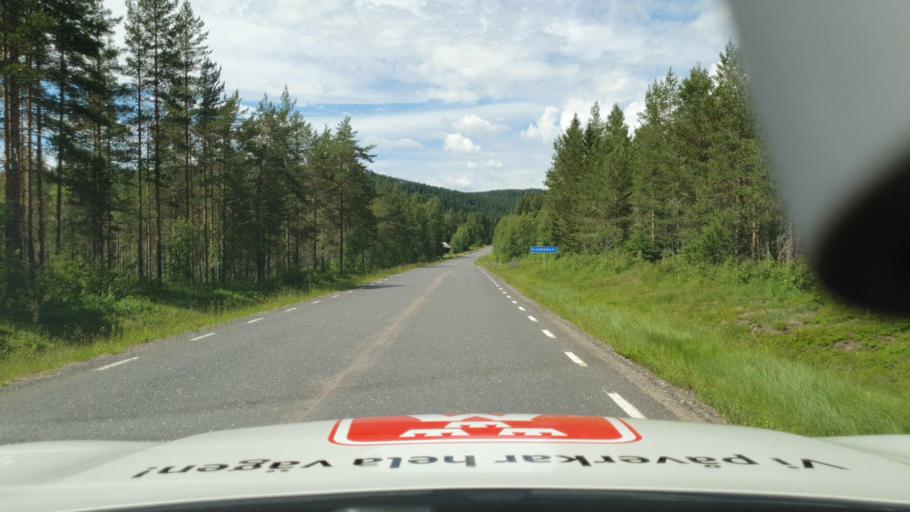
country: SE
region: Vaermland
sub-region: Torsby Kommun
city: Torsby
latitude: 60.5663
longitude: 12.7476
